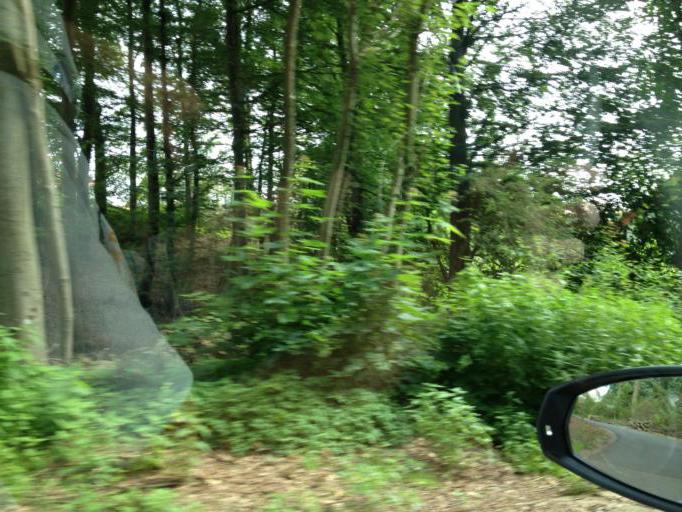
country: DE
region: Saarland
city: Losheim
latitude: 49.5101
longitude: 6.7267
